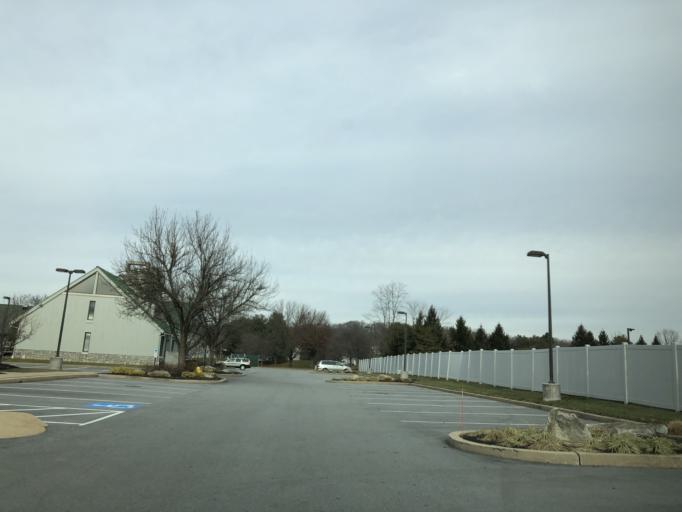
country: US
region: Pennsylvania
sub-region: Chester County
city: Exton
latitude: 40.0268
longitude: -75.6401
